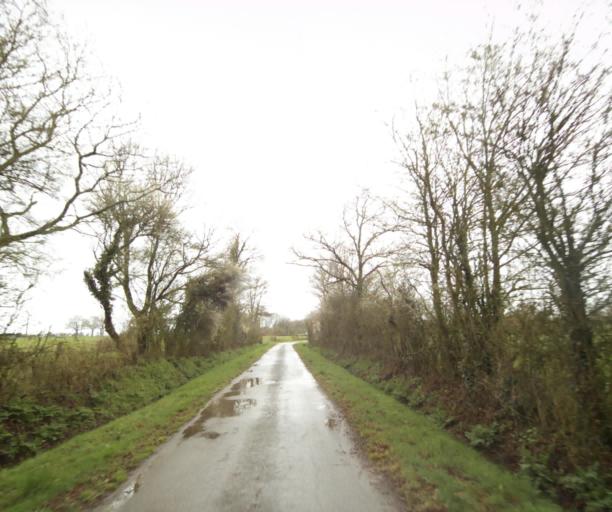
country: FR
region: Pays de la Loire
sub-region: Departement de la Loire-Atlantique
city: Bouvron
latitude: 47.4583
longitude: -1.8902
